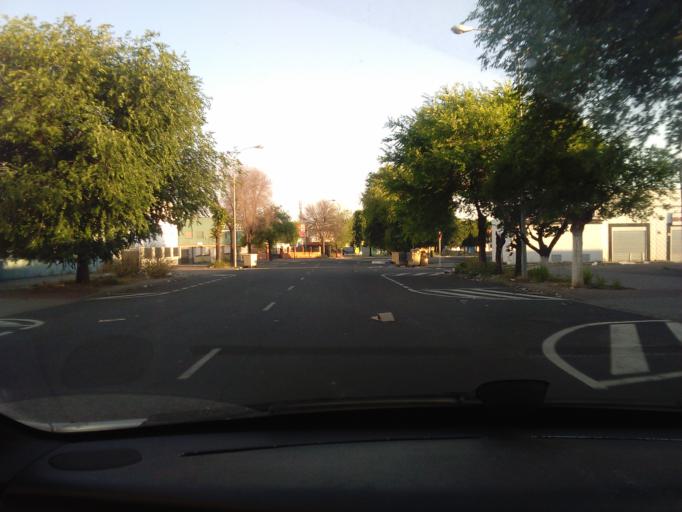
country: ES
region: Andalusia
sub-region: Provincia de Sevilla
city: Sevilla
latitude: 37.3945
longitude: -5.9392
